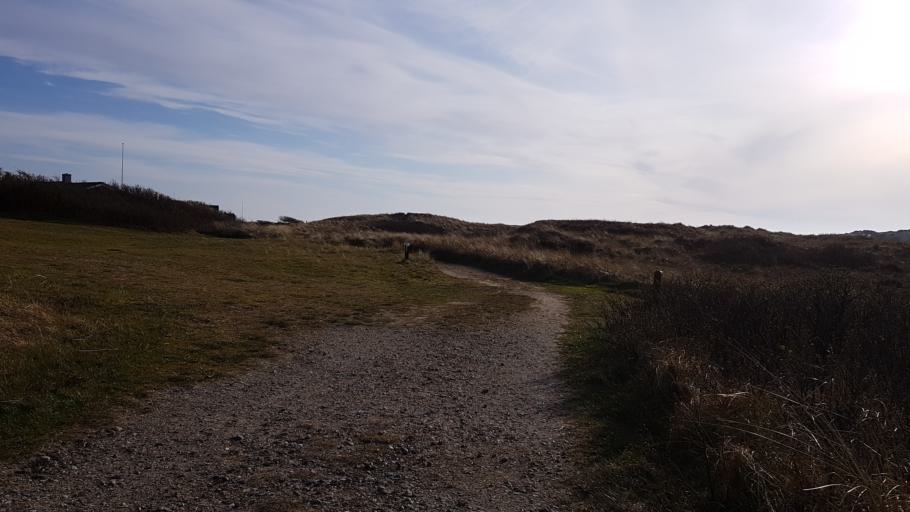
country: DE
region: Schleswig-Holstein
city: List
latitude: 55.1401
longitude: 8.4917
